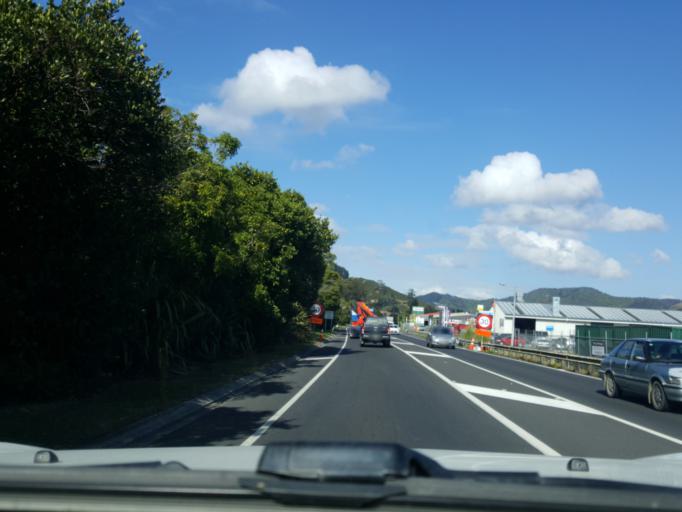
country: NZ
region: Waikato
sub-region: Waikato District
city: Ngaruawahia
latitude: -37.5706
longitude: 175.1583
